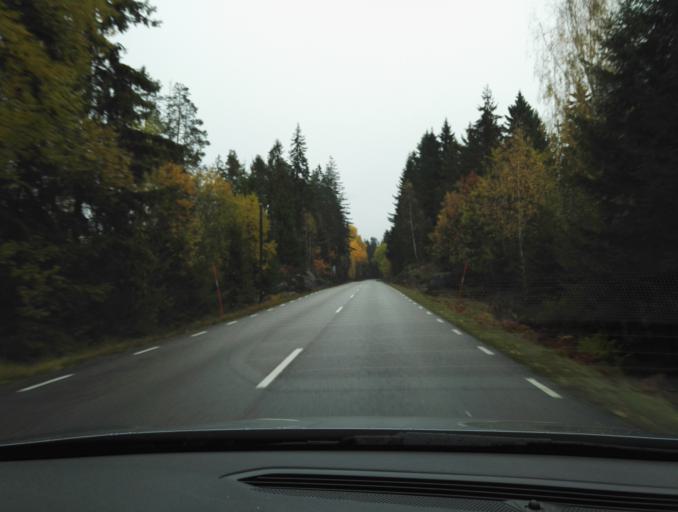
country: SE
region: Kronoberg
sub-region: Vaxjo Kommun
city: Rottne
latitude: 57.0284
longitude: 14.8218
